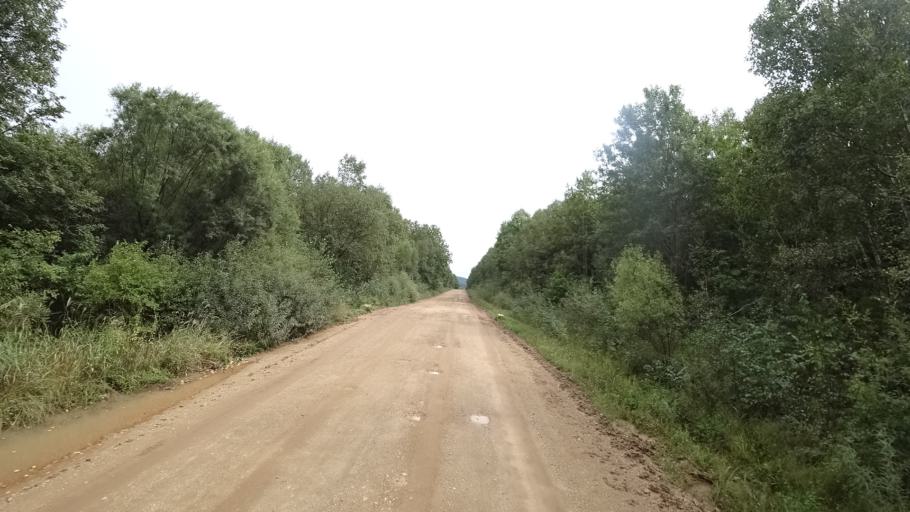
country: RU
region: Primorskiy
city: Lyalichi
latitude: 44.0866
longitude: 132.4389
